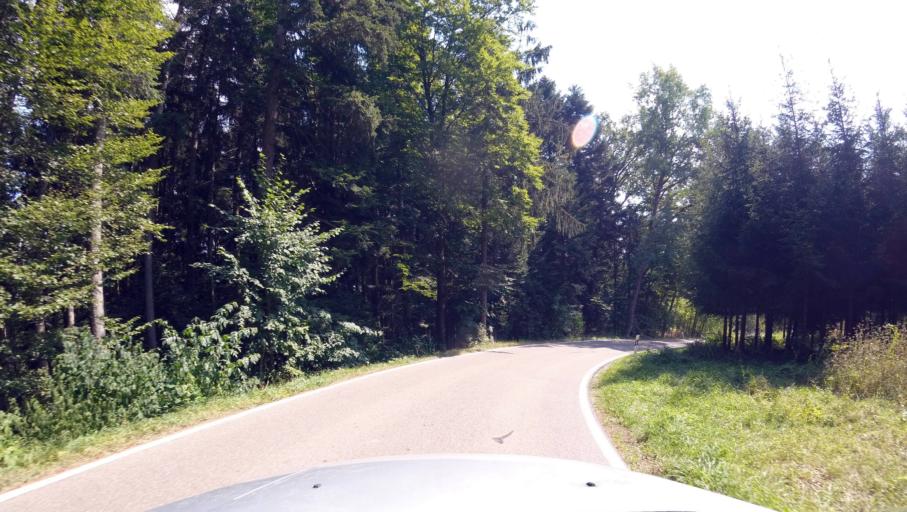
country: DE
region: Baden-Wuerttemberg
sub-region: Regierungsbezirk Stuttgart
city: Alfdorf
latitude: 48.8729
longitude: 9.6983
